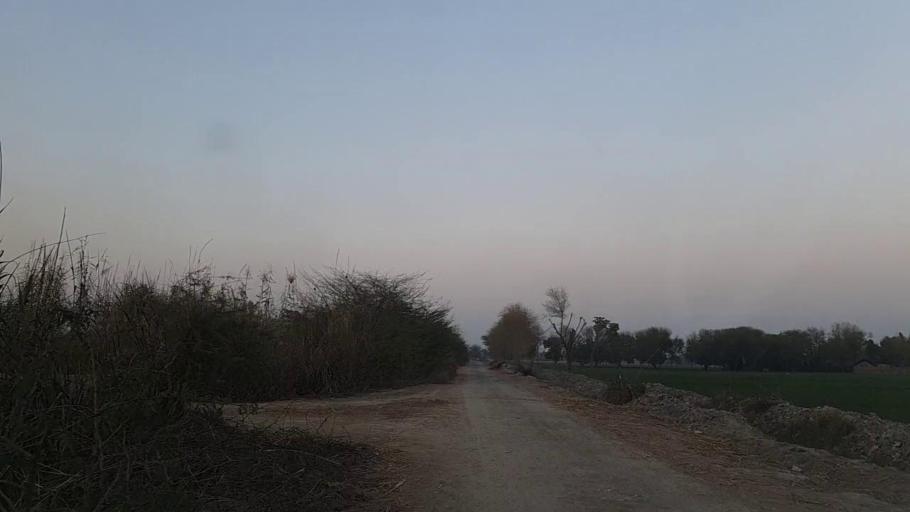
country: PK
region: Sindh
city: Bandhi
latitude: 26.6092
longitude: 68.3751
